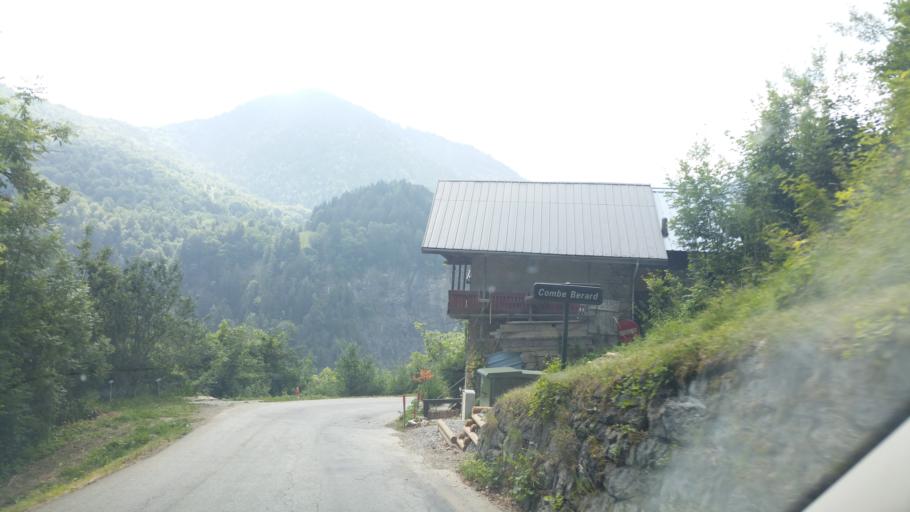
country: FR
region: Rhone-Alpes
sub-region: Departement de la Savoie
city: Saint-Jean-de-Maurienne
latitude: 45.2262
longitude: 6.3095
